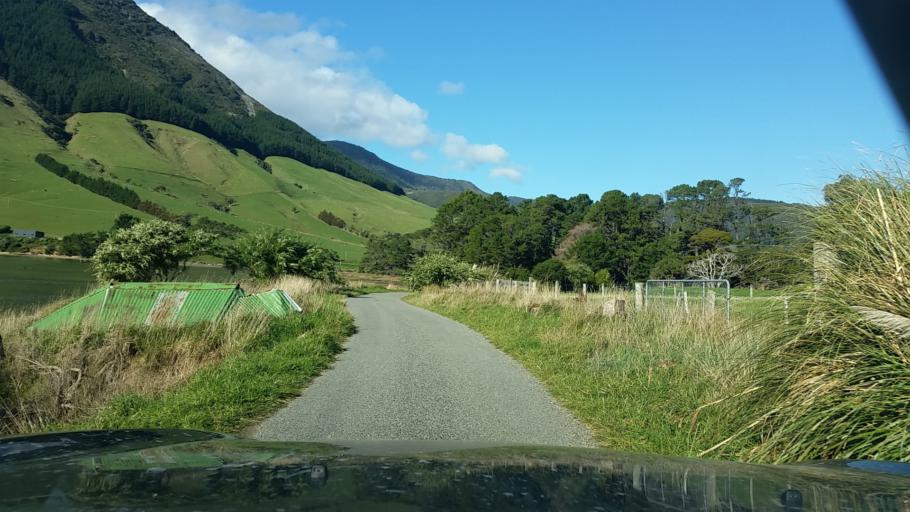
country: NZ
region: Marlborough
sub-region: Marlborough District
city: Picton
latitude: -41.1114
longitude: 174.0337
